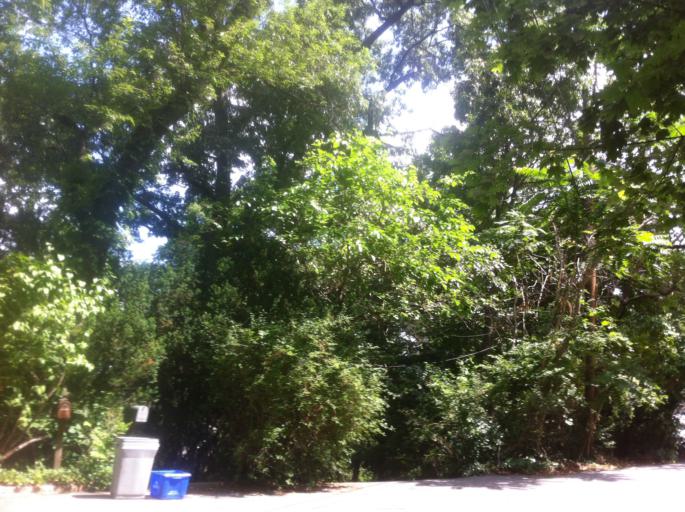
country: US
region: New York
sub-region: Nassau County
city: Sea Cliff
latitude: 40.8531
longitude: -73.6421
